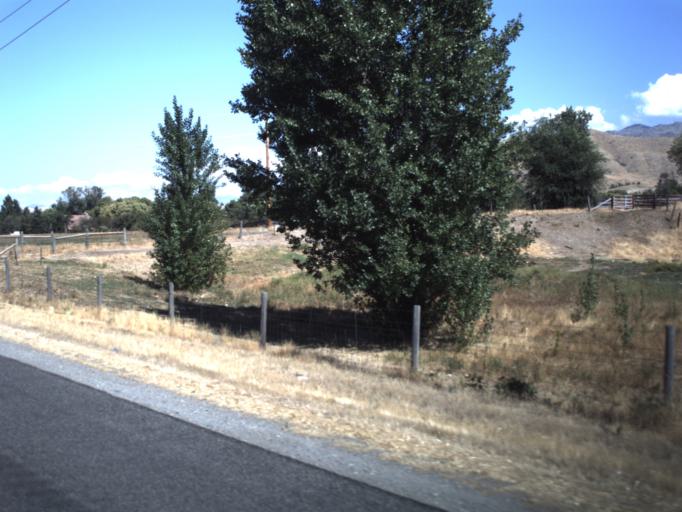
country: US
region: Utah
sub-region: Cache County
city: Richmond
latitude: 41.9516
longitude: -111.8132
